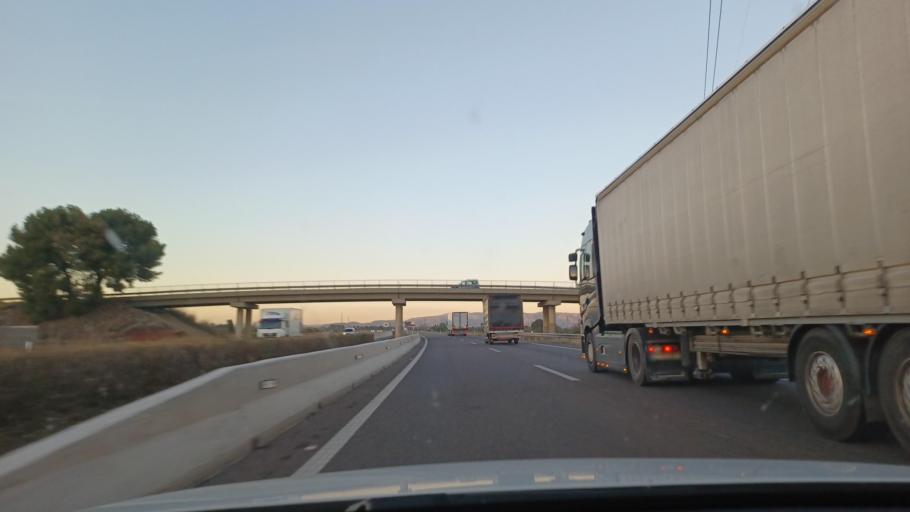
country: ES
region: Valencia
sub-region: Provincia de Castello
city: Vila-real
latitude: 39.9345
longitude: -0.1344
